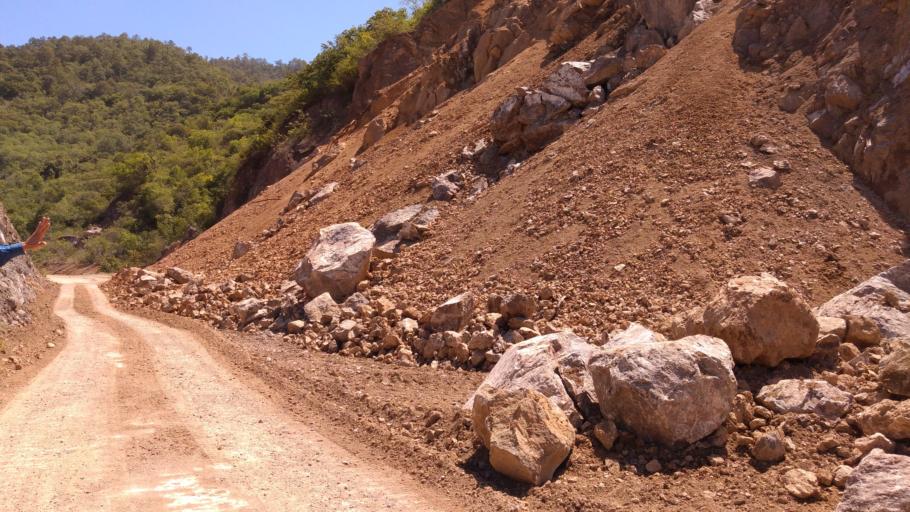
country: MX
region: Oaxaca
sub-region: San Pedro Quiatoni
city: San Pedro Quiatoni
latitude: 16.8356
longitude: -95.9747
